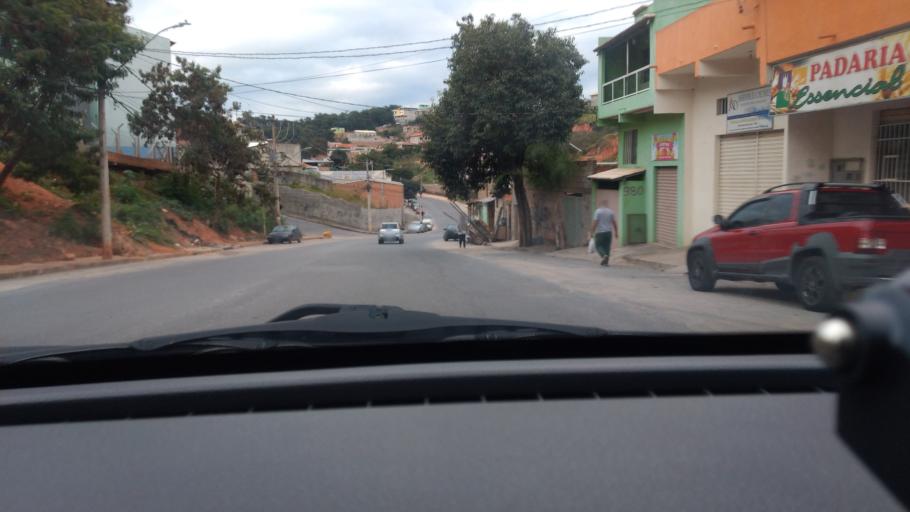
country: BR
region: Minas Gerais
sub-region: Santa Luzia
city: Santa Luzia
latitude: -19.8191
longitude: -43.9382
